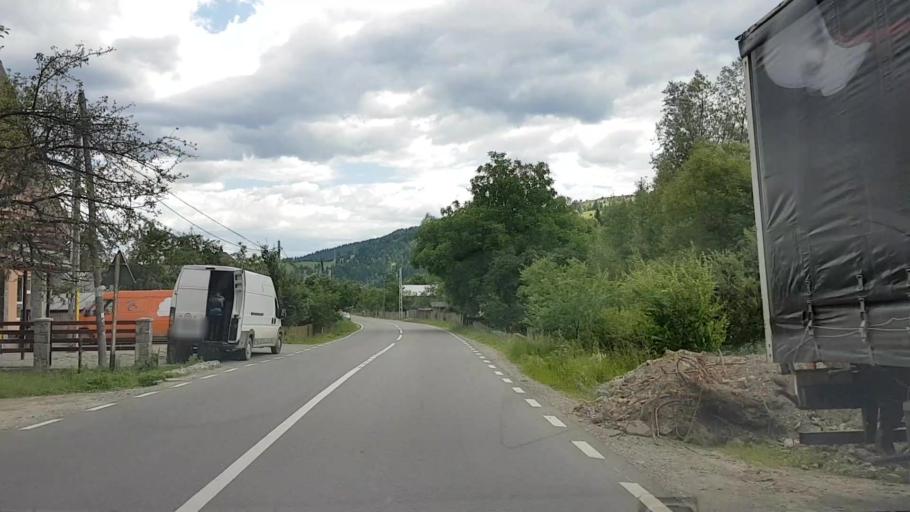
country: RO
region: Neamt
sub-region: Comuna Farcasa
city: Farcasa
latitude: 47.1645
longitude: 25.8102
